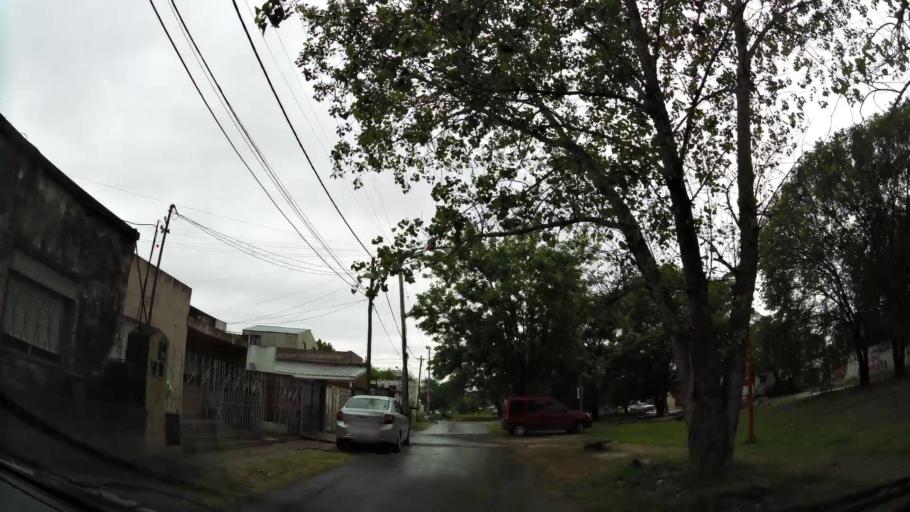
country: AR
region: Buenos Aires
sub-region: Partido de Quilmes
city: Quilmes
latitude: -34.7629
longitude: -58.2307
